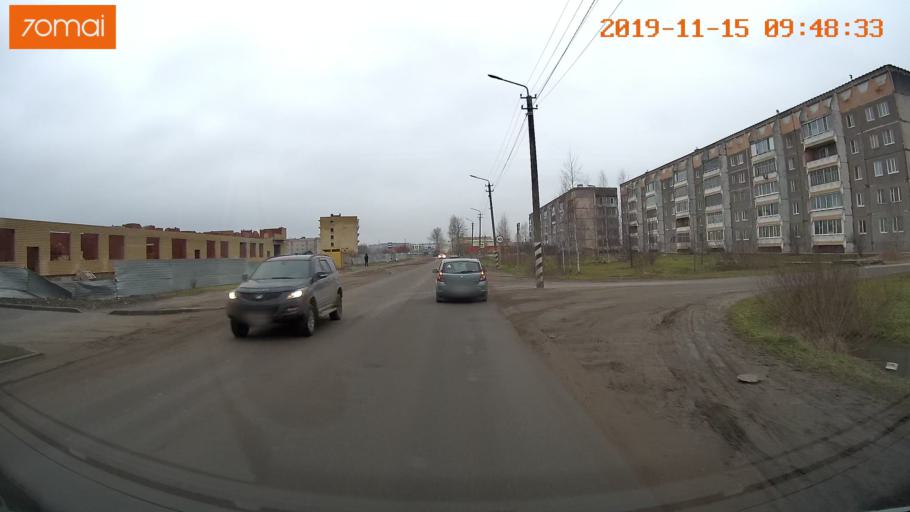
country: RU
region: Vologda
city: Sheksna
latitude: 59.2237
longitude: 38.5131
